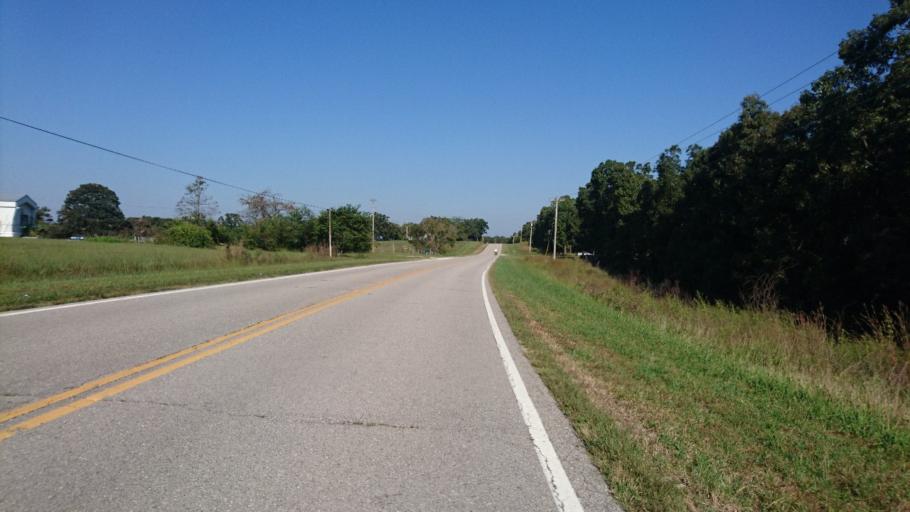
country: US
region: Missouri
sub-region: Pulaski County
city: Richland
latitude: 37.7462
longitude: -92.3584
